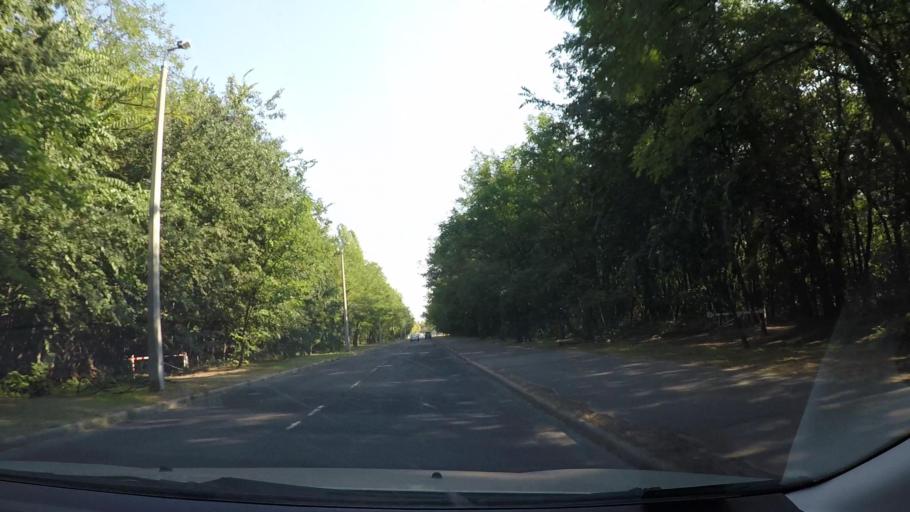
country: HU
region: Budapest
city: Budapest XV. keruelet
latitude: 47.5920
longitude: 19.1138
